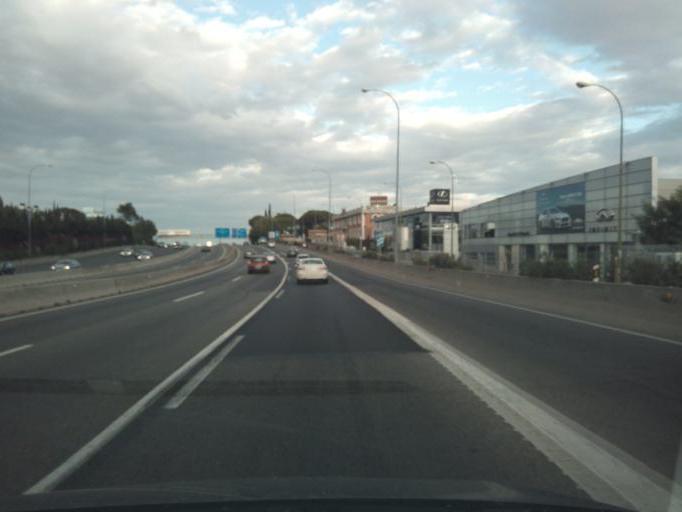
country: ES
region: Madrid
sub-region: Provincia de Madrid
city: Pozuelo de Alarcon
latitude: 40.4668
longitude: -3.8114
